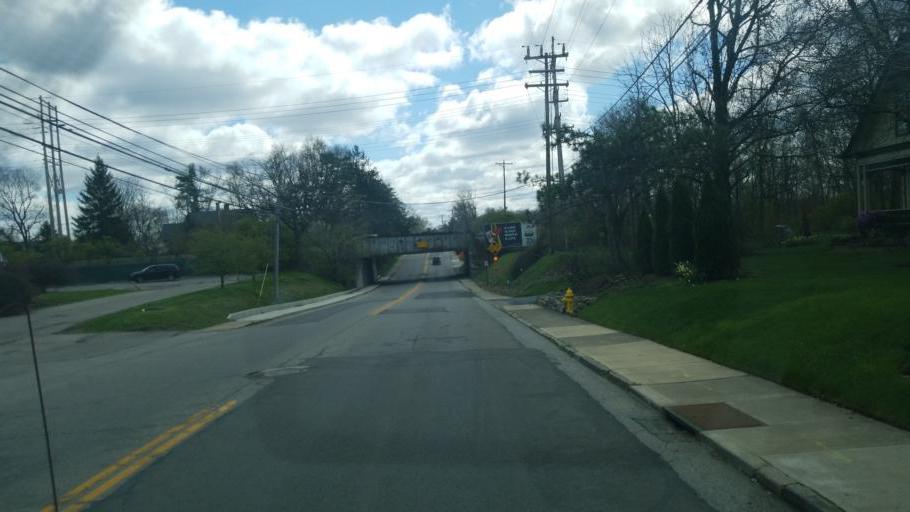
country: US
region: Ohio
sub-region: Delaware County
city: Delaware
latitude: 40.3043
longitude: -83.0837
